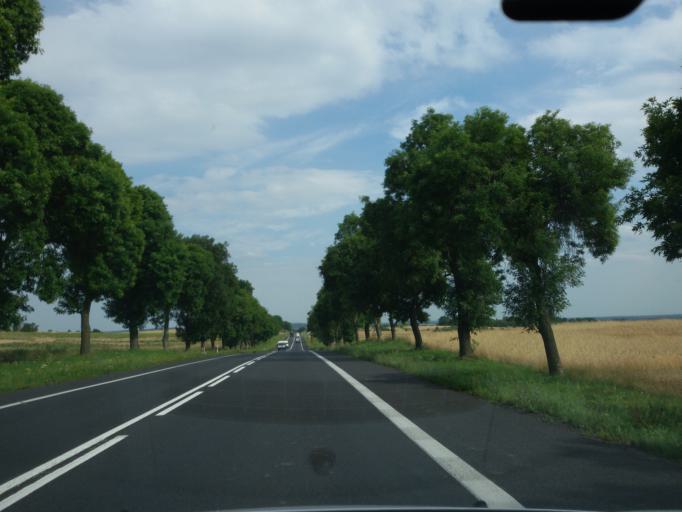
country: PL
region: Lower Silesian Voivodeship
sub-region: Powiat polkowicki
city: Gaworzyce
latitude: 51.6400
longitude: 15.8829
